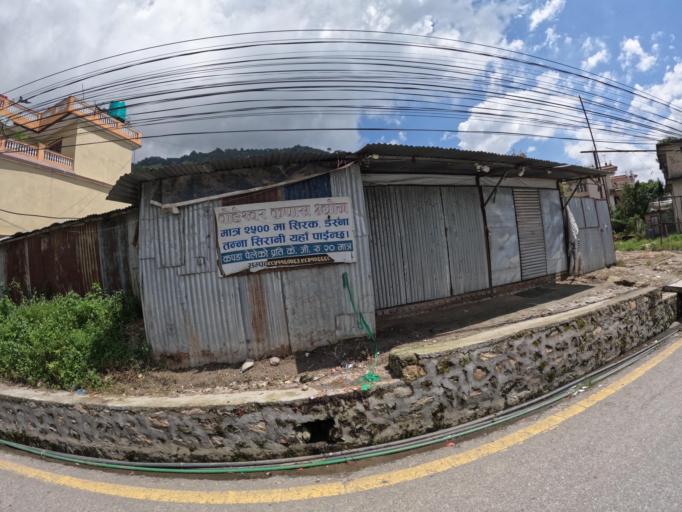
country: NP
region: Central Region
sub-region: Bagmati Zone
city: Kathmandu
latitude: 27.7911
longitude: 85.3302
